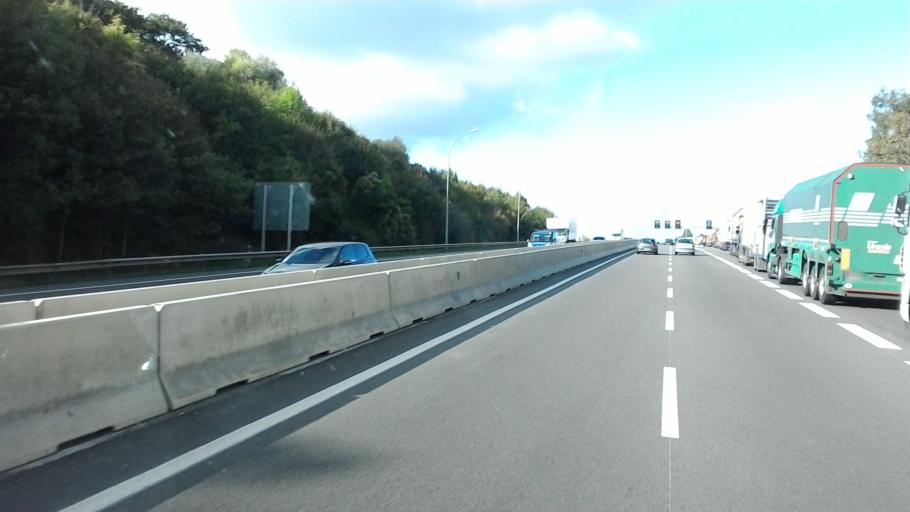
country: LU
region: Luxembourg
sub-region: Canton d'Esch-sur-Alzette
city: Dudelange
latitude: 49.4739
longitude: 6.1214
